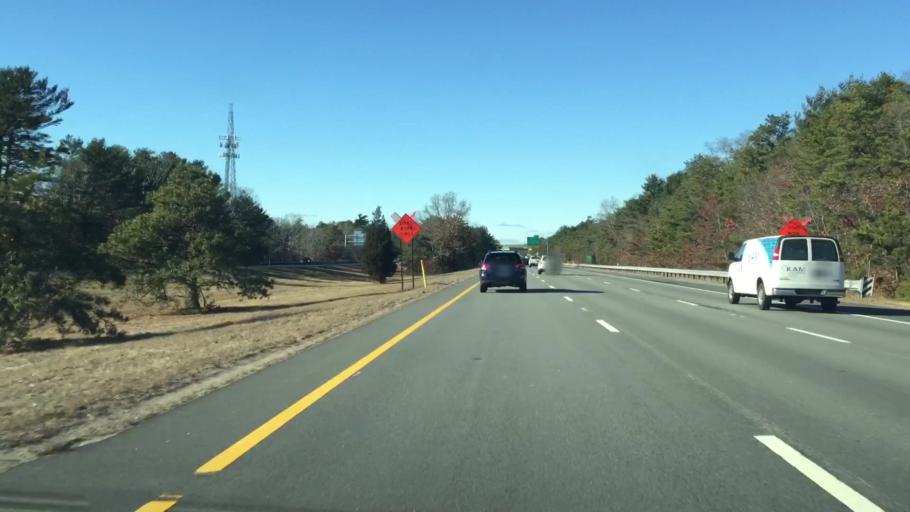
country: US
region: Massachusetts
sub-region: Plymouth County
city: Wareham Center
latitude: 41.7735
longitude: -70.6981
